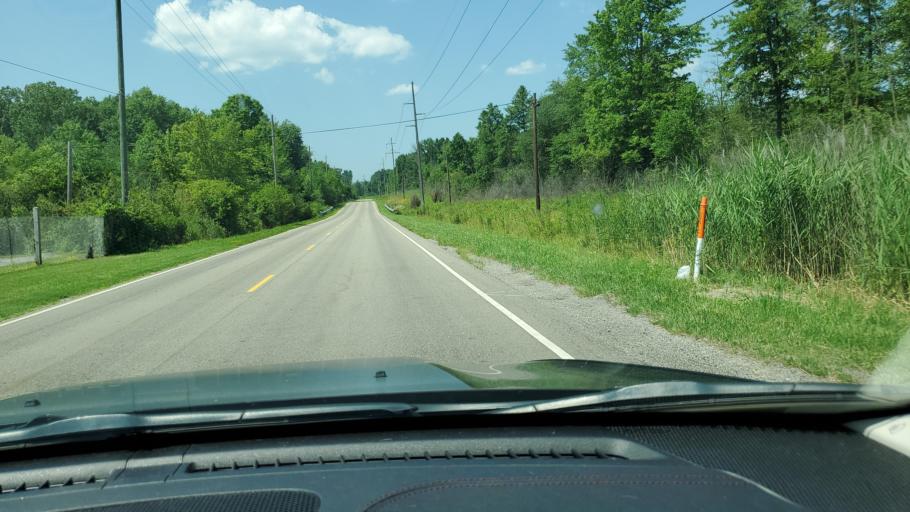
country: US
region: Ohio
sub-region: Trumbull County
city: Bolindale
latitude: 41.1973
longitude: -80.7908
